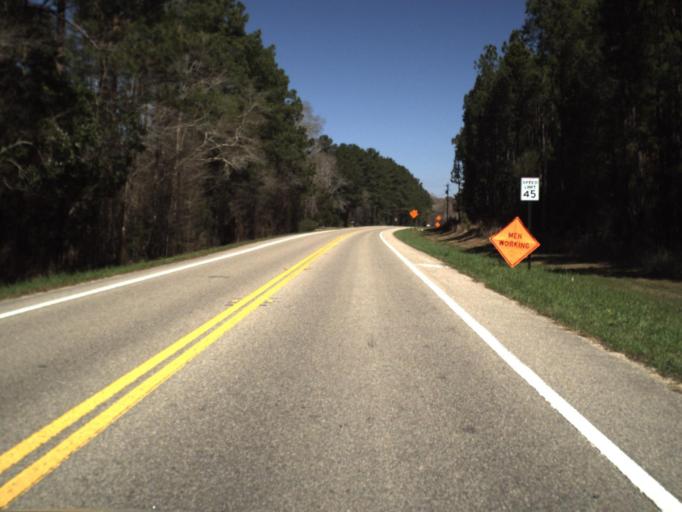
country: US
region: Florida
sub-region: Calhoun County
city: Blountstown
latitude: 30.5223
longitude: -85.0309
